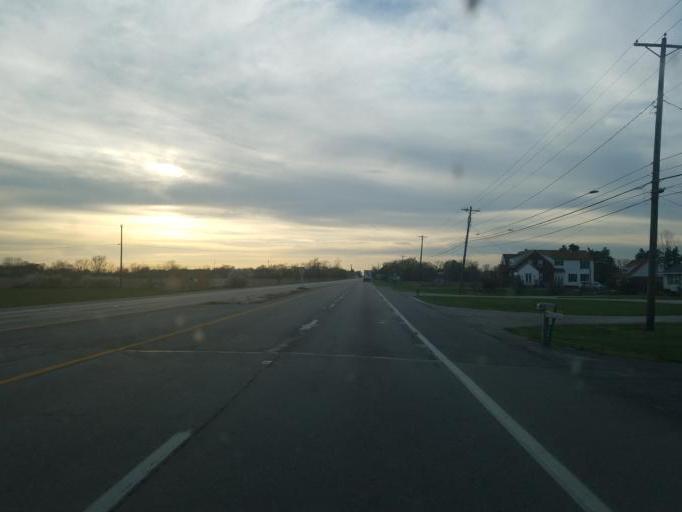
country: US
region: Ohio
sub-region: Sandusky County
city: Woodville
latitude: 41.4461
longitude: -83.3527
